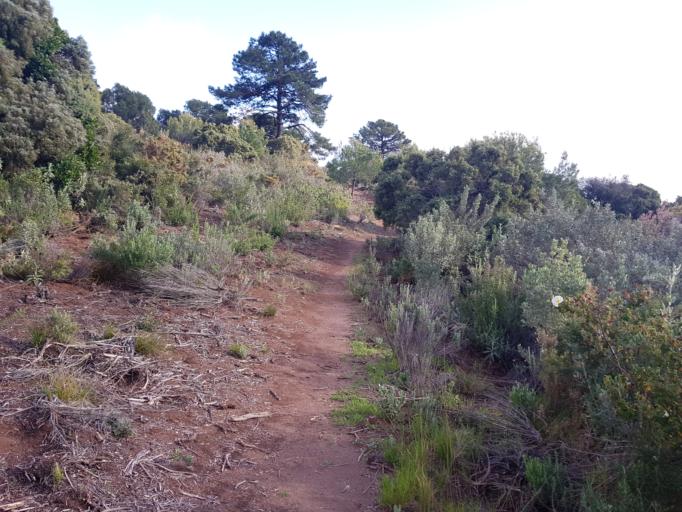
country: ES
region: Andalusia
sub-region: Provincia de Malaga
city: Marbella
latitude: 36.5527
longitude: -4.8940
